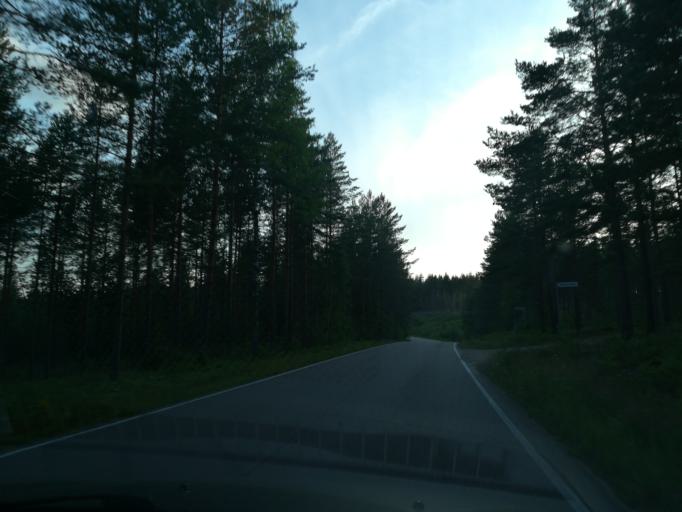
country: FI
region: South Karelia
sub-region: Lappeenranta
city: Joutseno
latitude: 61.3499
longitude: 28.4496
